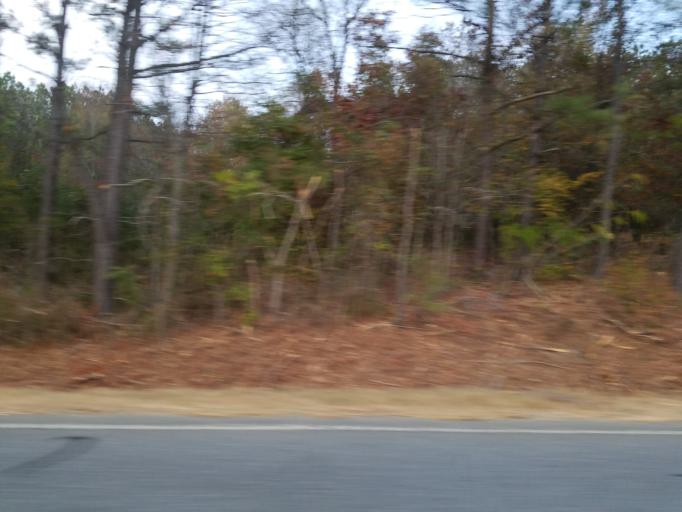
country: US
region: Georgia
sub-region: Murray County
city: Chatsworth
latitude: 34.5921
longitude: -84.7474
